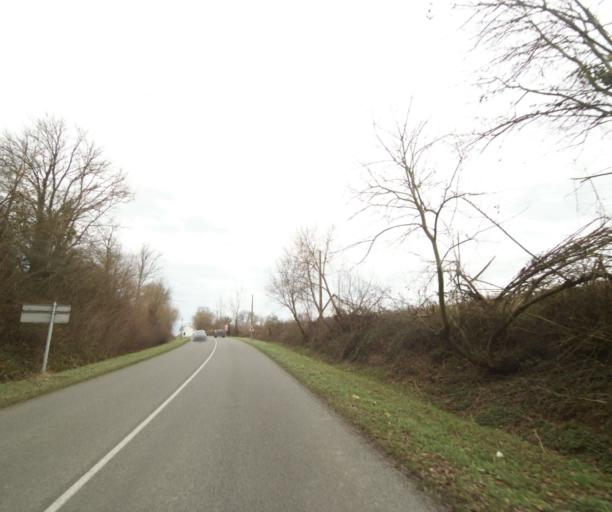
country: FR
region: Nord-Pas-de-Calais
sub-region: Departement du Nord
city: Sebourg
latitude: 50.3369
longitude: 3.6373
